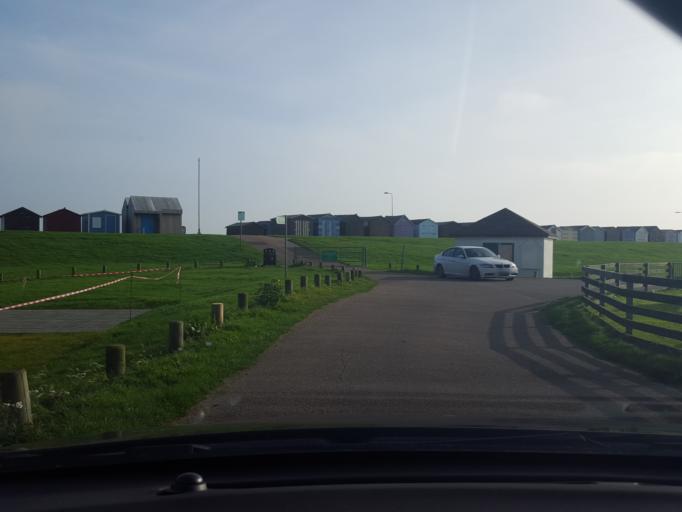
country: GB
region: England
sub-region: Essex
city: Dovercourt
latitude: 51.9270
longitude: 1.2707
